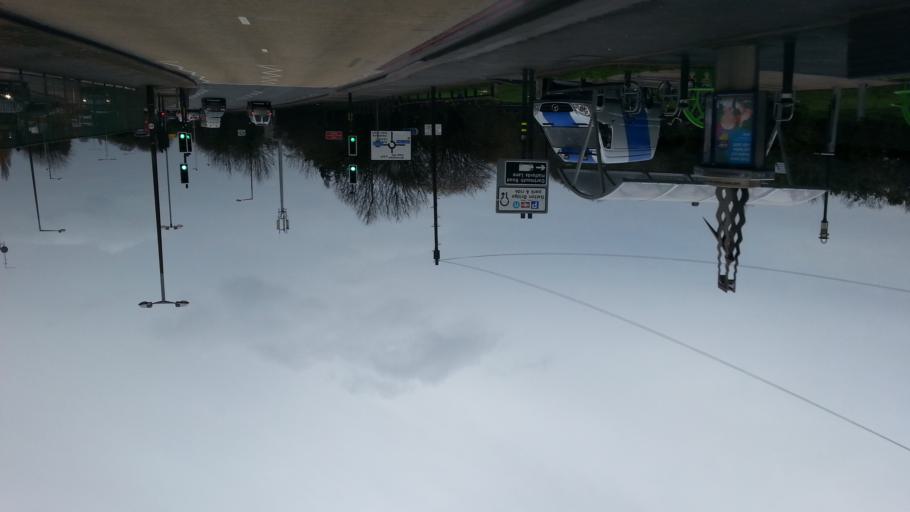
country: GB
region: England
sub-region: Sandwell
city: Smethwick
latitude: 52.5017
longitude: -1.9807
